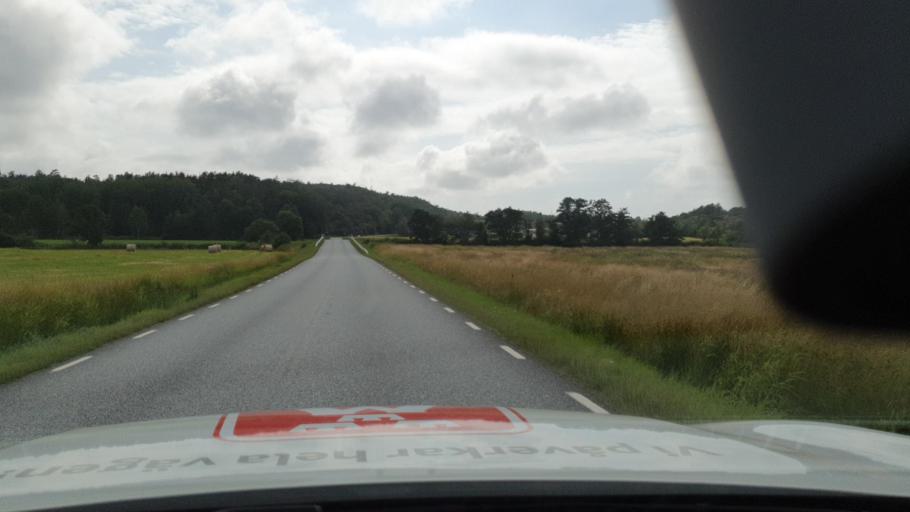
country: SE
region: Vaestra Goetaland
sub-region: Sotenas Kommun
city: Hunnebostrand
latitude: 58.5720
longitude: 11.3144
